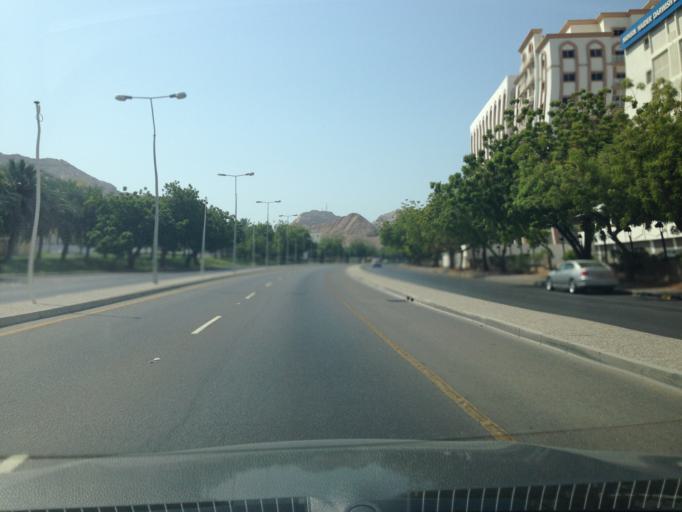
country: OM
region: Muhafazat Masqat
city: Muscat
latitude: 23.5982
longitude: 58.5388
